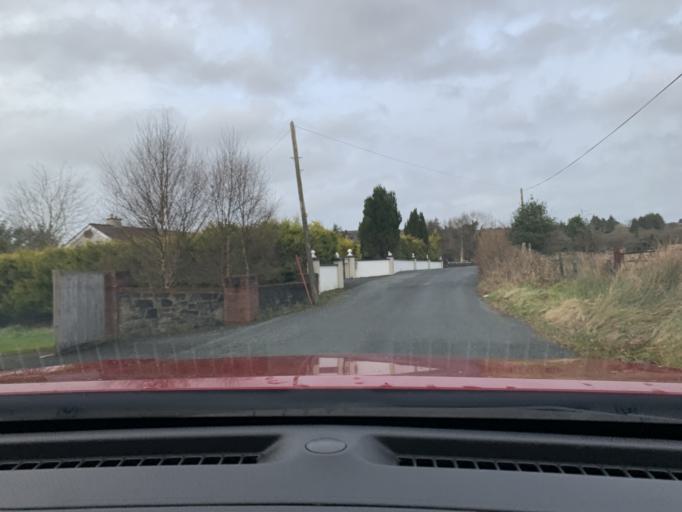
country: IE
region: Connaught
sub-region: Roscommon
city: Boyle
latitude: 53.9767
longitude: -8.4182
